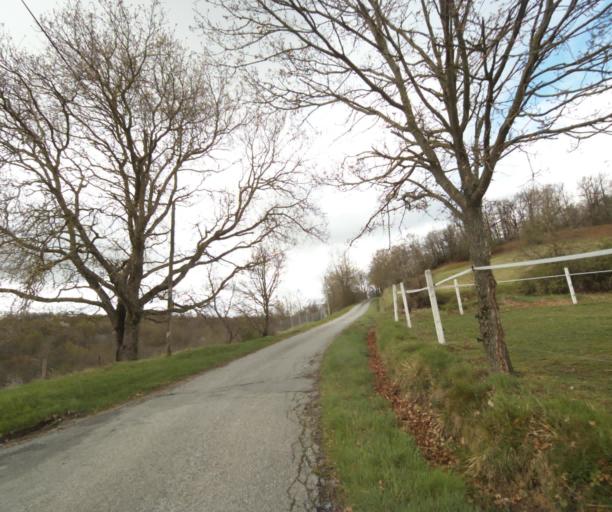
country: FR
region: Midi-Pyrenees
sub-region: Departement de l'Ariege
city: Saverdun
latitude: 43.2232
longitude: 1.5485
